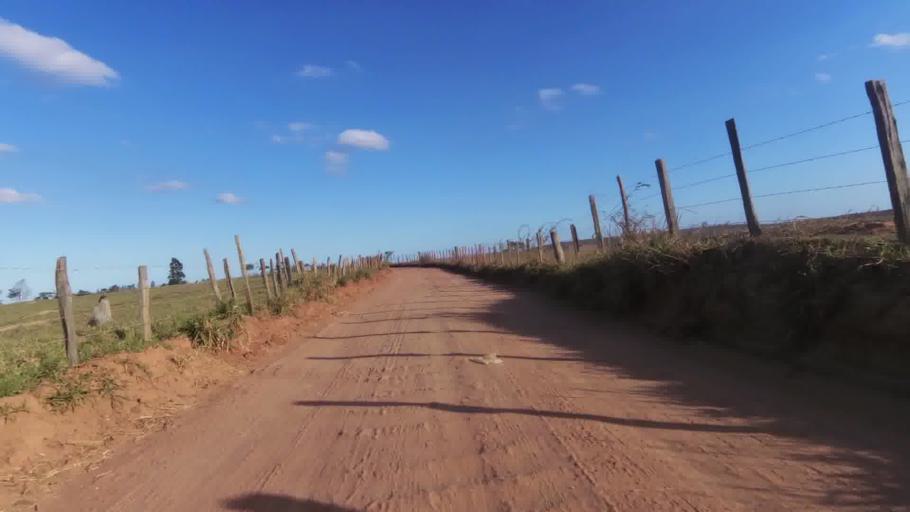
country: BR
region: Espirito Santo
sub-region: Marataizes
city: Marataizes
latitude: -21.1548
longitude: -41.0611
